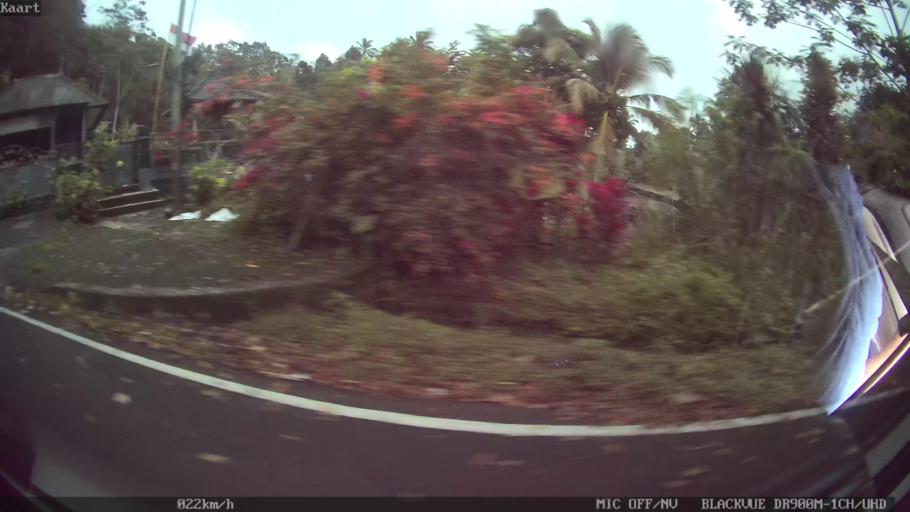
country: ID
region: Bali
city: Peneng
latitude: -8.3690
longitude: 115.2158
